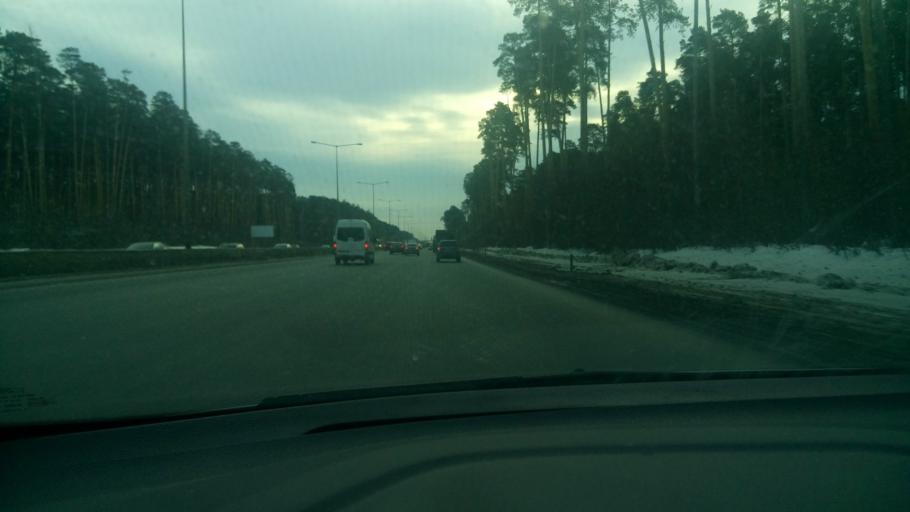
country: RU
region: Sverdlovsk
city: Yekaterinburg
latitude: 56.7935
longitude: 60.6586
